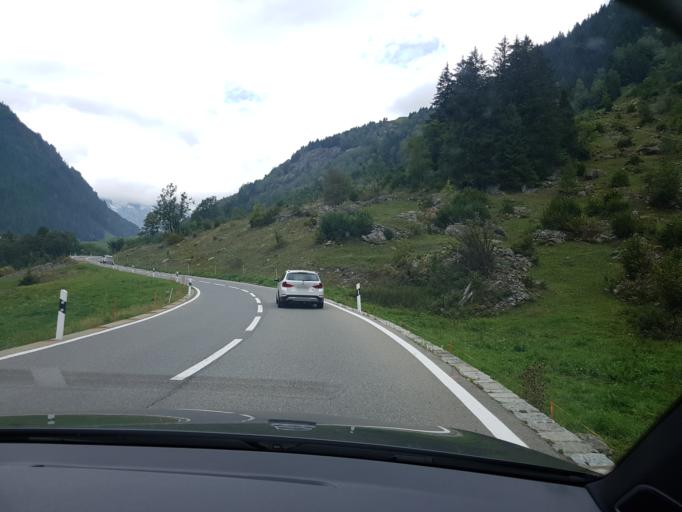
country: CH
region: Uri
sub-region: Uri
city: Andermatt
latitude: 46.7200
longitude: 8.5712
